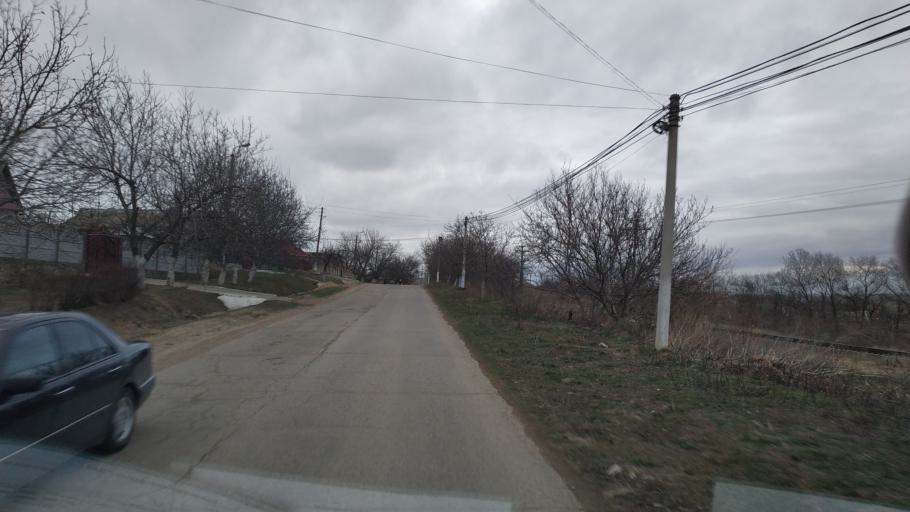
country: MD
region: Bender
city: Bender
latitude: 46.7704
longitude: 29.4818
